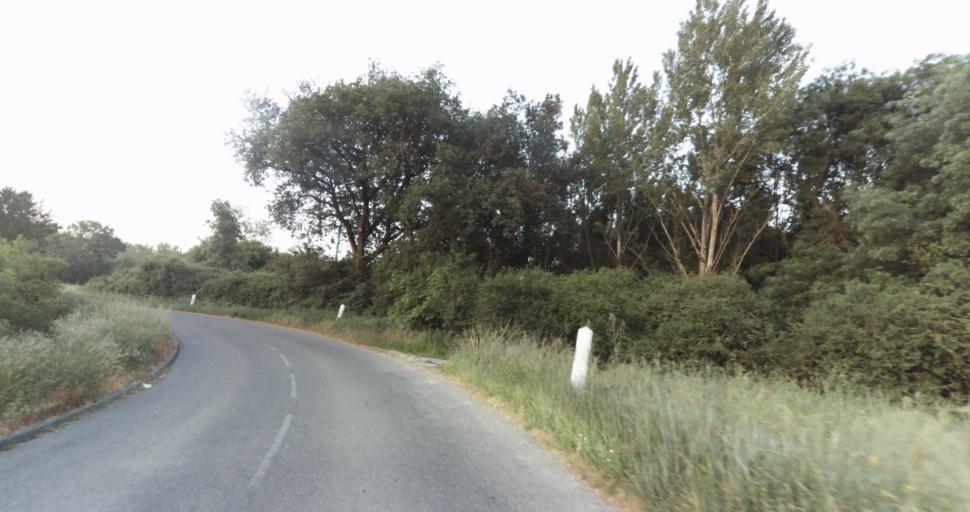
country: FR
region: Midi-Pyrenees
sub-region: Departement de la Haute-Garonne
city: Levignac
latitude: 43.6705
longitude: 1.1891
